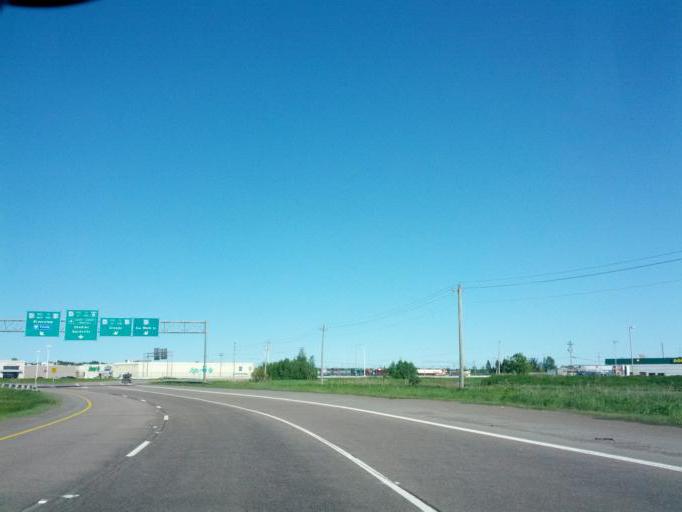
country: CA
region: New Brunswick
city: Moncton
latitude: 46.0959
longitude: -64.7679
